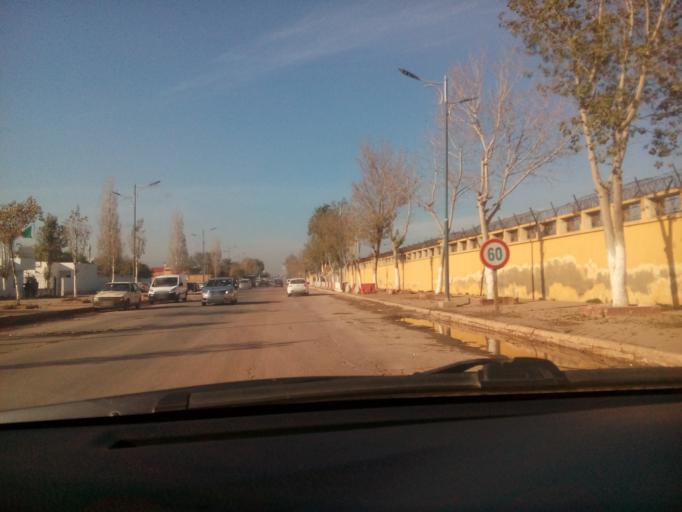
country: DZ
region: Oran
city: Es Senia
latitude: 35.6530
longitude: -0.6141
